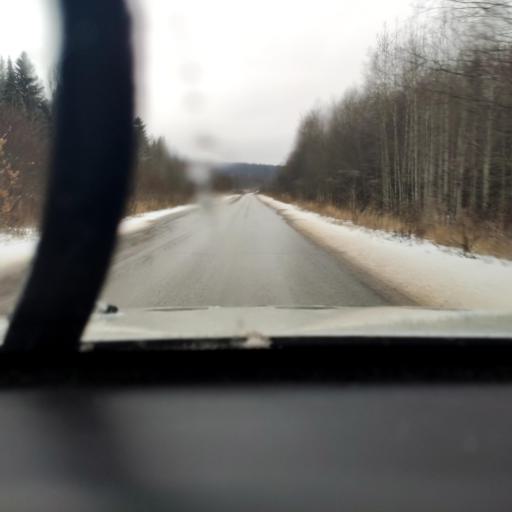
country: RU
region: Perm
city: Ferma
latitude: 57.9827
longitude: 56.3622
